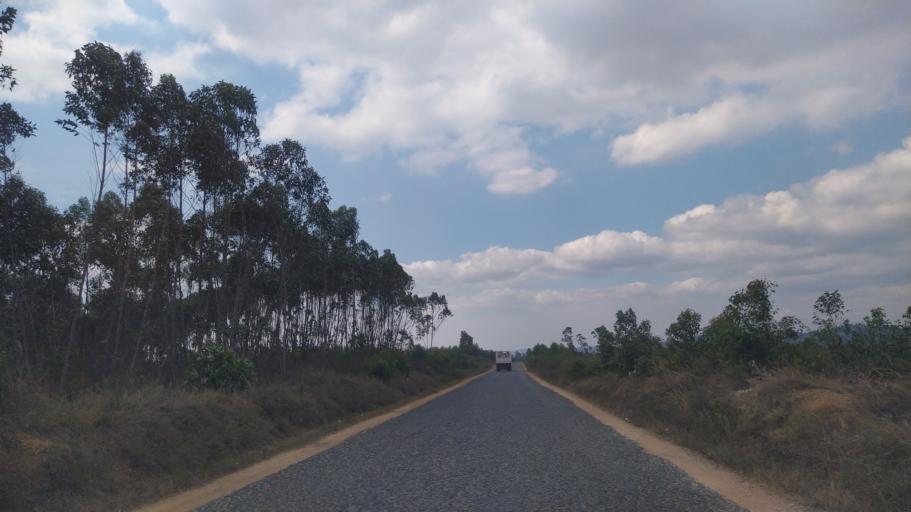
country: MG
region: Alaotra Mangoro
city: Moramanga
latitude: -18.7728
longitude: 48.2506
